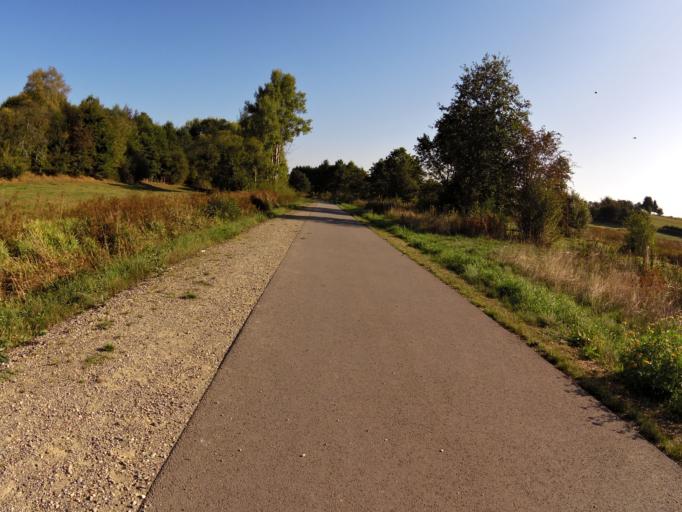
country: BE
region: Wallonia
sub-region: Province de Liege
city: Ambleve
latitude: 50.3505
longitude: 6.1241
